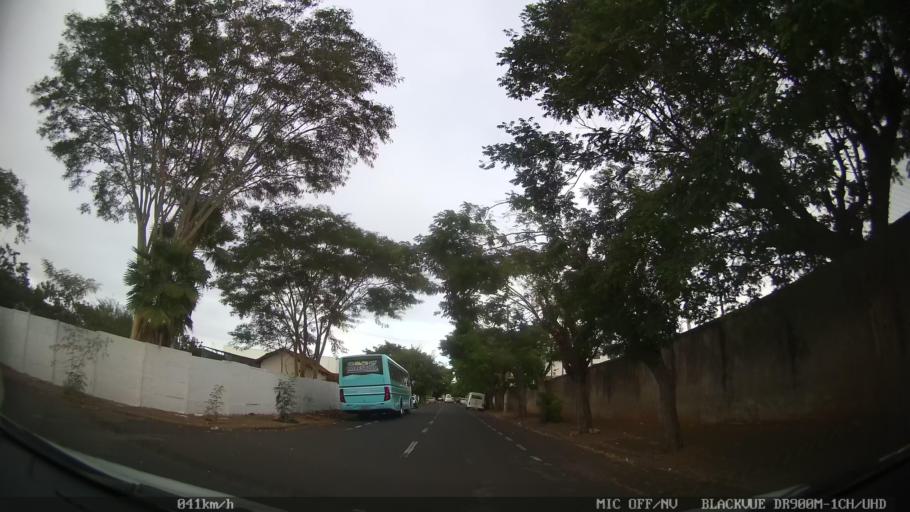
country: BR
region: Sao Paulo
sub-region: Sao Jose Do Rio Preto
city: Sao Jose do Rio Preto
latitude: -20.8330
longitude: -49.3964
